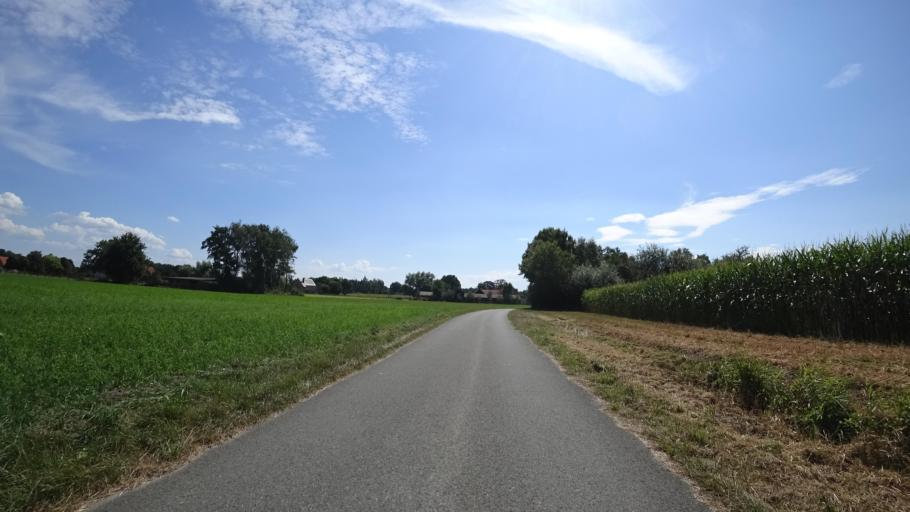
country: DE
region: North Rhine-Westphalia
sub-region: Regierungsbezirk Detmold
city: Guetersloh
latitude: 51.9517
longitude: 8.3883
